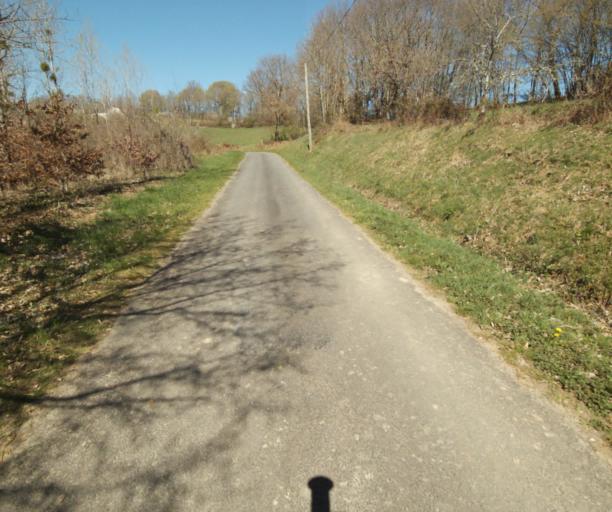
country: FR
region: Limousin
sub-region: Departement de la Correze
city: Saint-Mexant
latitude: 45.2872
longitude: 1.6997
